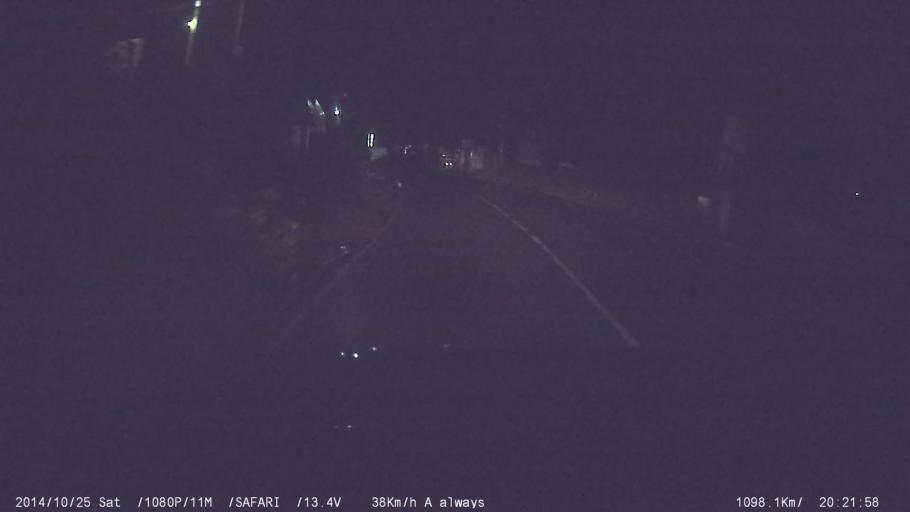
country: IN
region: Kerala
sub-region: Kottayam
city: Palackattumala
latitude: 9.7484
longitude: 76.5608
